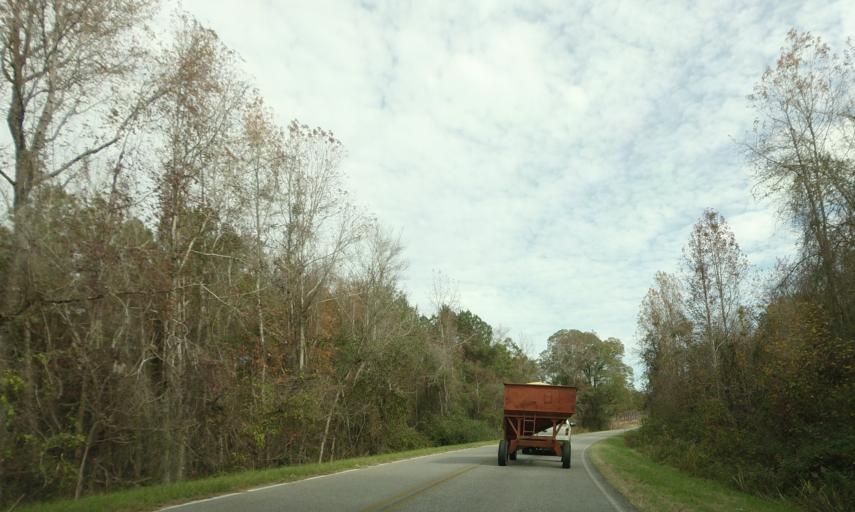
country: US
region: Georgia
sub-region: Dodge County
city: Chester
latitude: 32.4662
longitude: -83.1206
